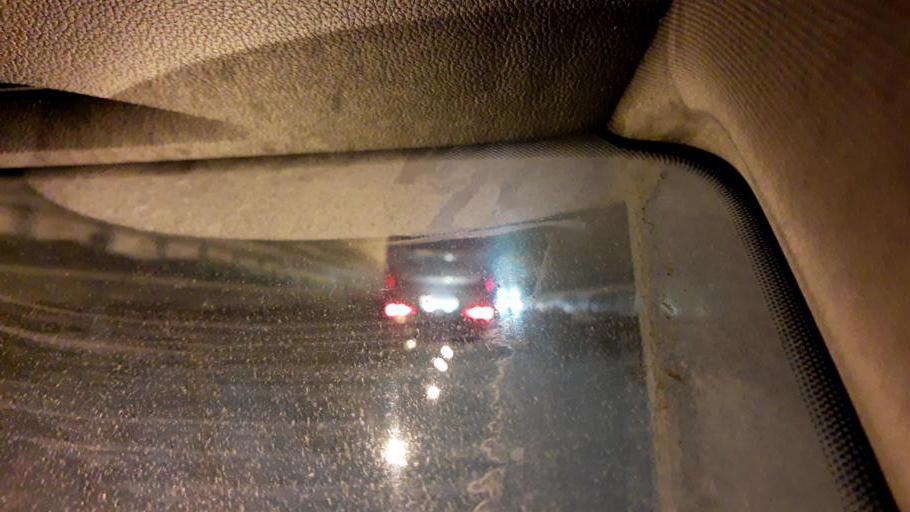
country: RU
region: Moskovskaya
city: Elektrostal'
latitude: 55.7839
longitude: 38.4320
